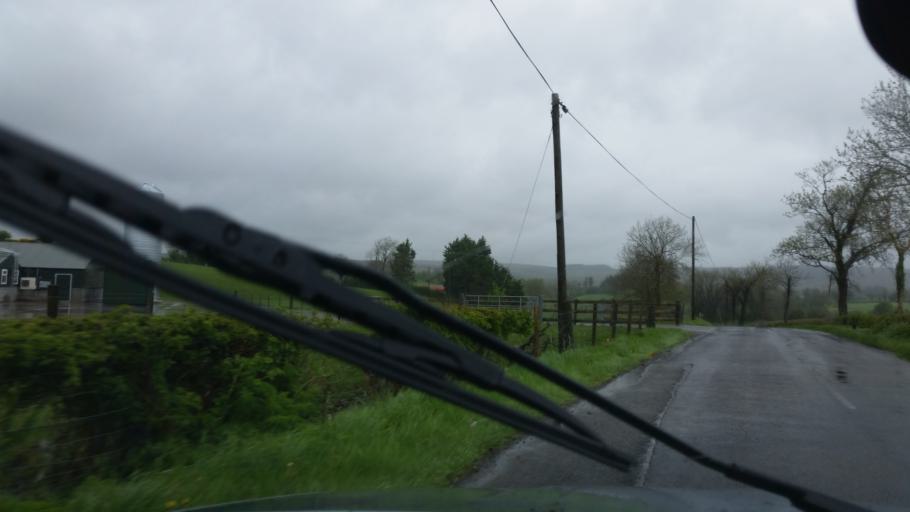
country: GB
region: Northern Ireland
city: Fivemiletown
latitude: 54.4077
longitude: -7.3204
